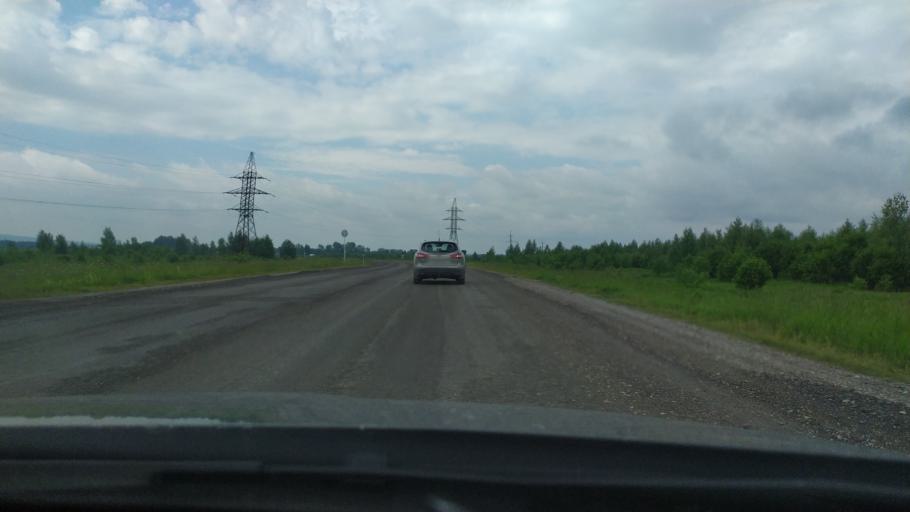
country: RU
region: Perm
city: Kalino
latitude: 58.2939
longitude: 57.4721
